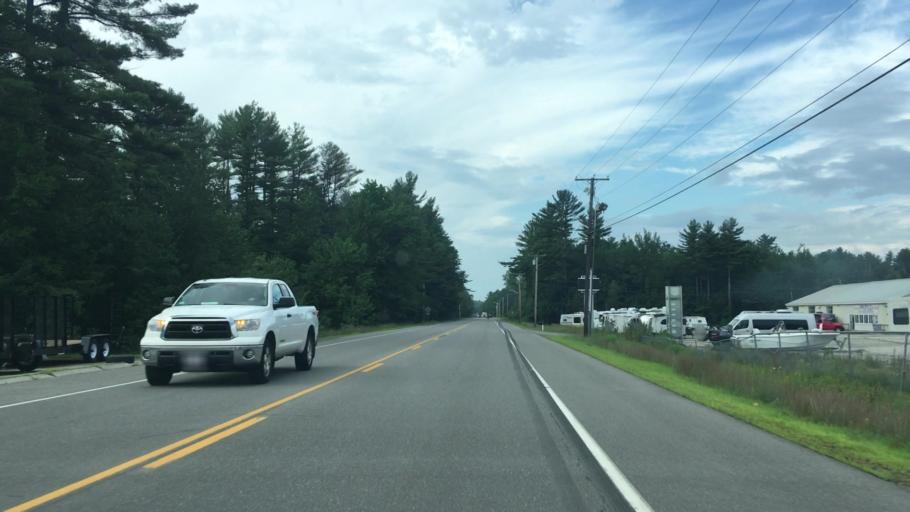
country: US
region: New Hampshire
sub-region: Strafford County
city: Rochester
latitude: 43.3479
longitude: -70.9308
